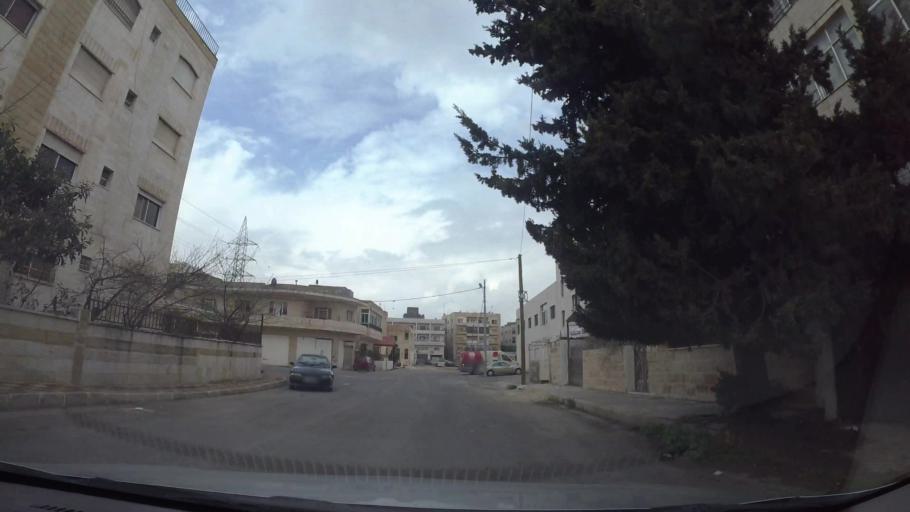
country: JO
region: Amman
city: Umm as Summaq
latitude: 31.8927
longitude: 35.8391
